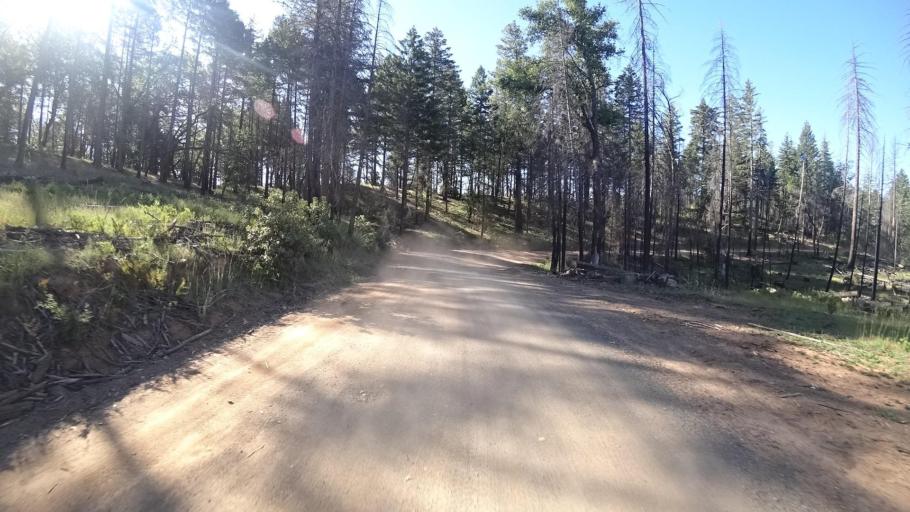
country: US
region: California
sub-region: Lake County
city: Upper Lake
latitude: 39.3845
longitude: -122.9833
